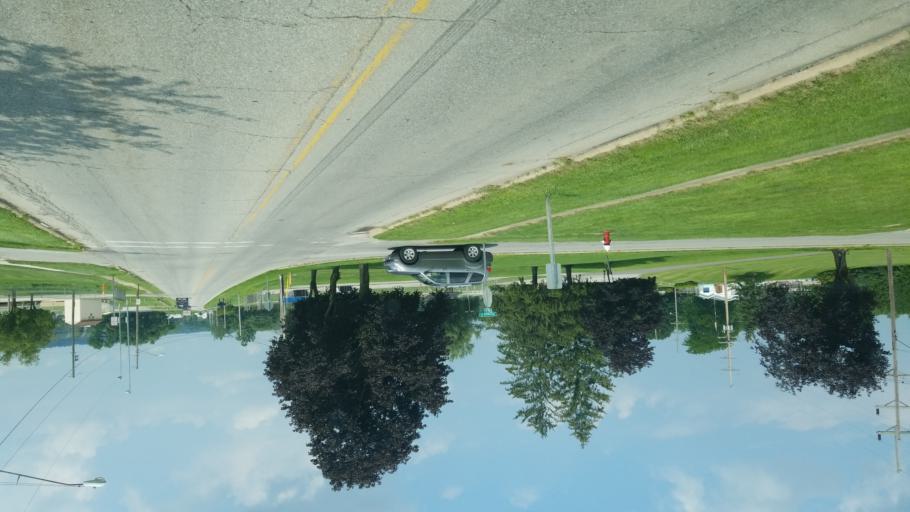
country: US
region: Ohio
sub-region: Richland County
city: Lexington
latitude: 40.6846
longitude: -82.5844
